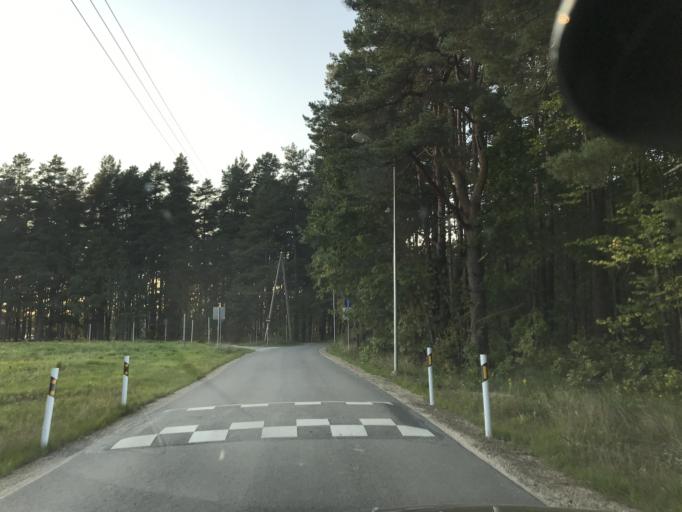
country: LV
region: Ikskile
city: Ikskile
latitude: 56.8248
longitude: 24.5098
